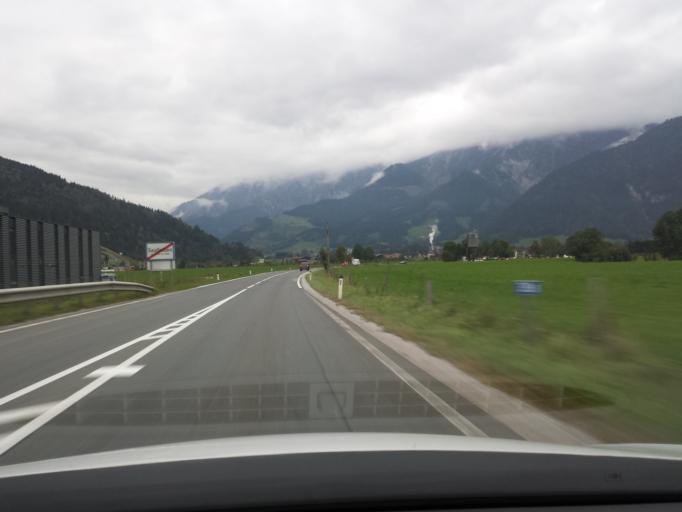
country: AT
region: Salzburg
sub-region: Politischer Bezirk Zell am See
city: Saalfelden am Steinernen Meer
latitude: 47.4314
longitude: 12.8306
